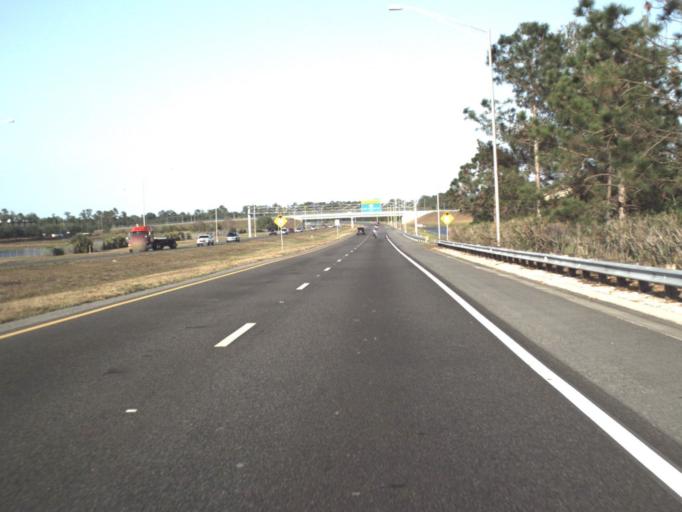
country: US
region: Florida
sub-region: Orange County
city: Alafaya
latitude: 28.5505
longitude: -81.2006
